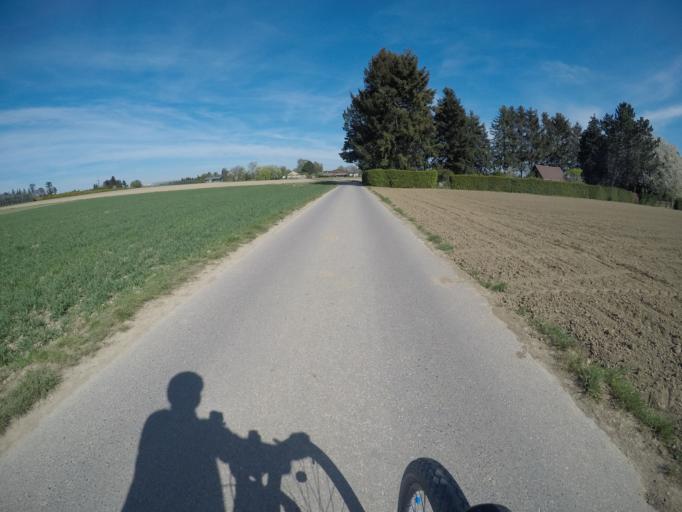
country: DE
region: Baden-Wuerttemberg
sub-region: Regierungsbezirk Stuttgart
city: Moglingen
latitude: 48.8594
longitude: 9.1318
